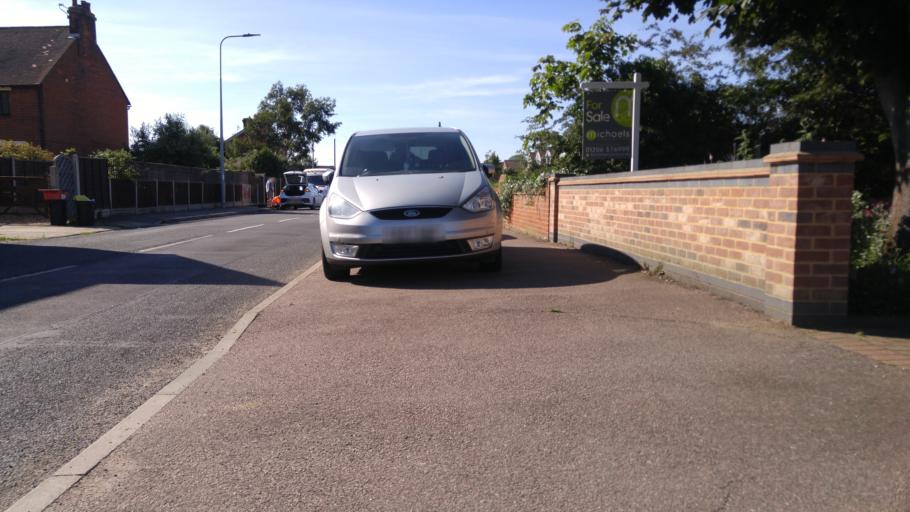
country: GB
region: England
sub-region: Essex
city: Rowhedge
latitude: 51.8663
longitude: 0.9306
